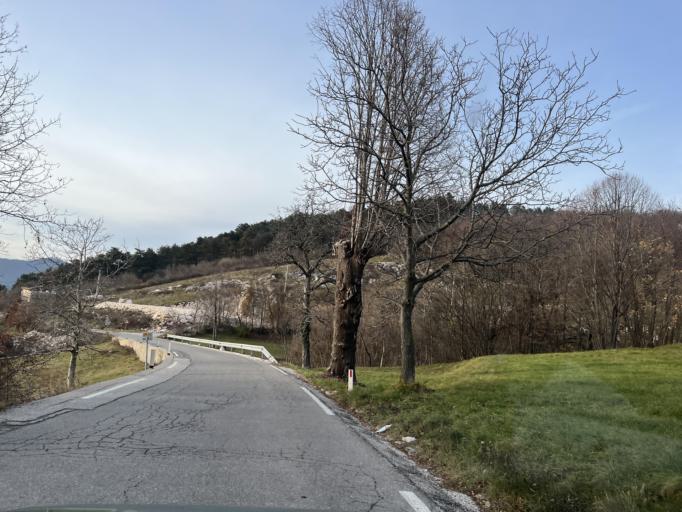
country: SI
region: Nova Gorica
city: Kromberk
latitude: 45.9841
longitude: 13.7116
